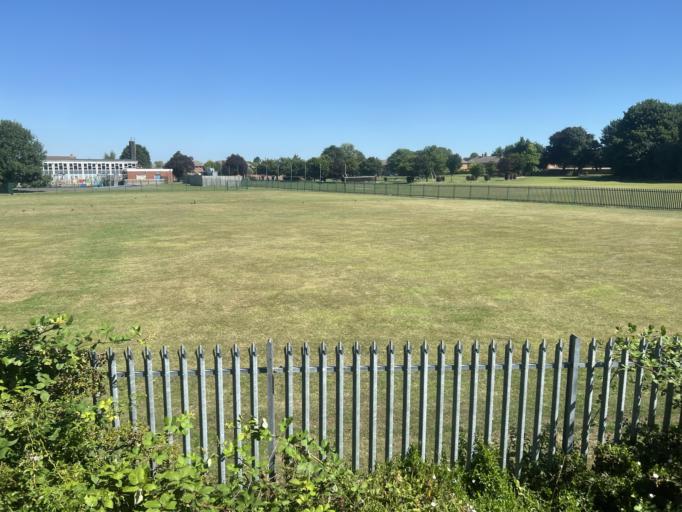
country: GB
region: England
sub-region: Lincolnshire
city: Wainfleet All Saints
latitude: 53.1063
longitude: 0.2321
